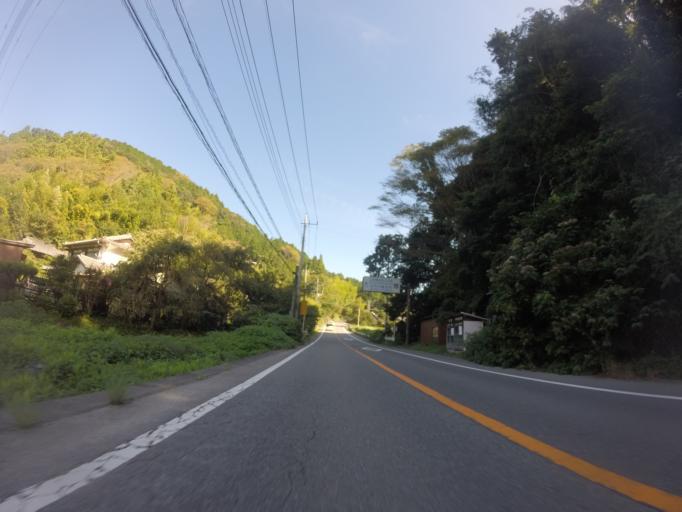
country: JP
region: Shizuoka
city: Fujinomiya
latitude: 35.3426
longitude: 138.4501
